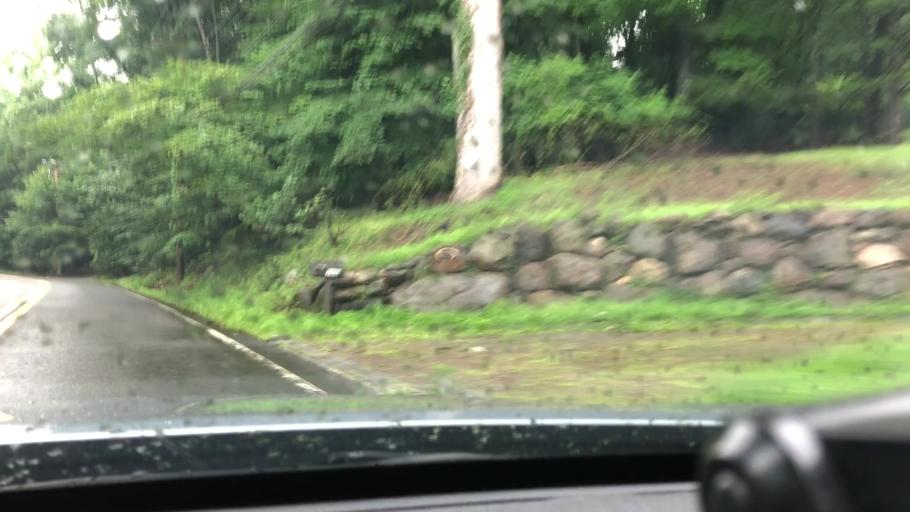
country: US
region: New Jersey
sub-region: Bergen County
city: Saddle River
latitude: 41.0325
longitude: -74.0871
